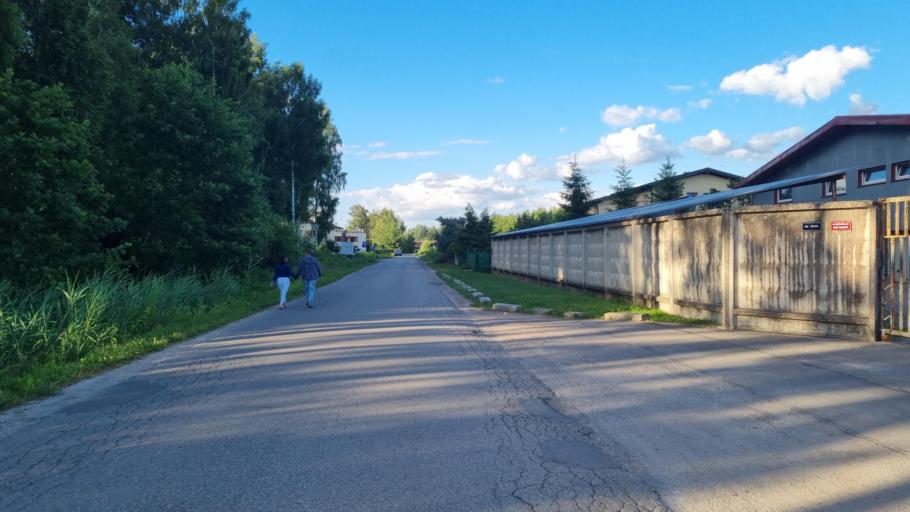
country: LV
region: Kekava
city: Balozi
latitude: 56.8733
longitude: 24.1479
